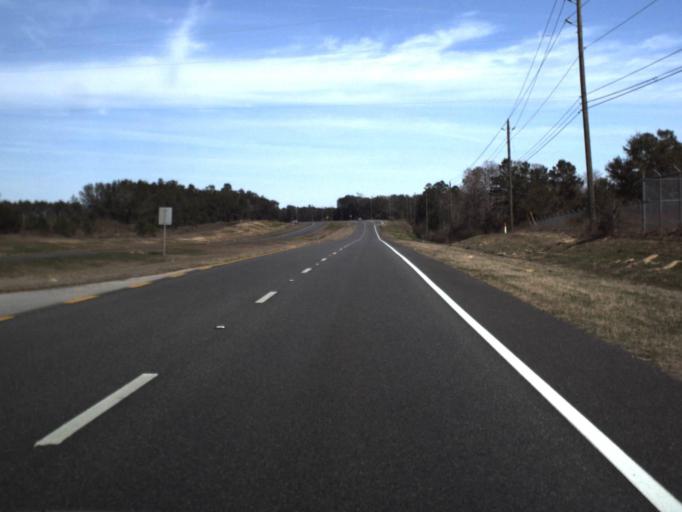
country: US
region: Florida
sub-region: Bay County
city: Lynn Haven
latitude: 30.4196
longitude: -85.6895
